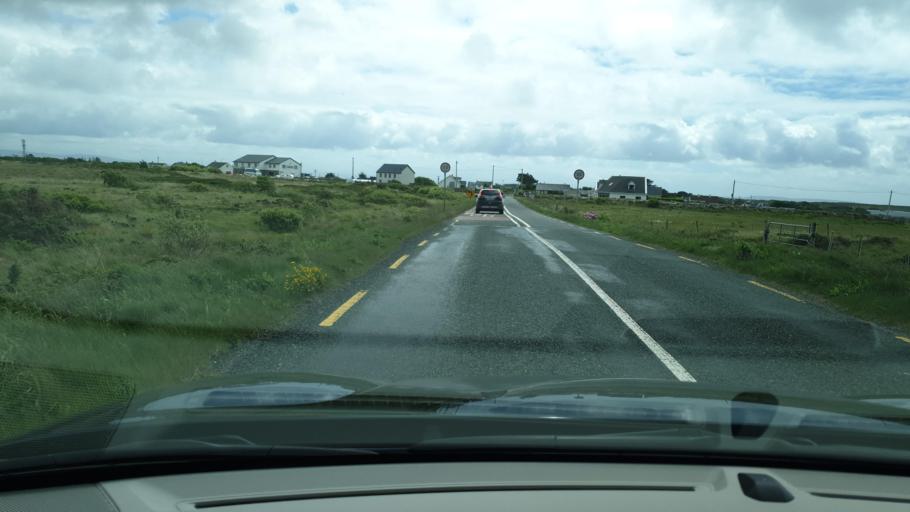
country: IE
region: Connaught
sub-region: County Galway
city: Oughterard
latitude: 53.2437
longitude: -9.5042
